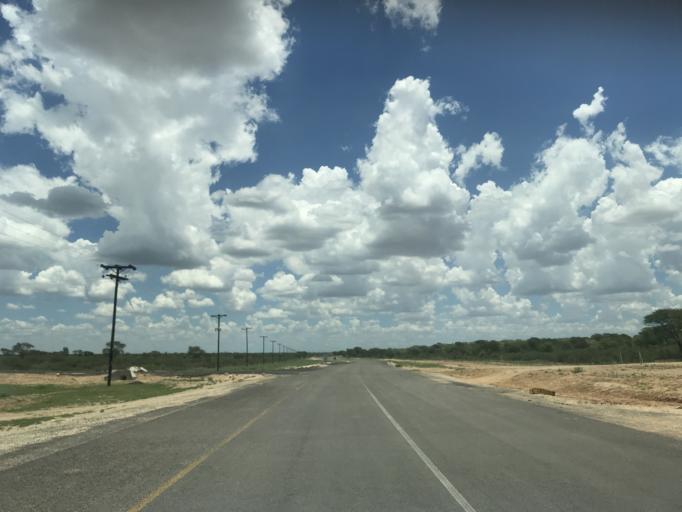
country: BW
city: Mabuli
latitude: -25.7884
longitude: 24.9009
